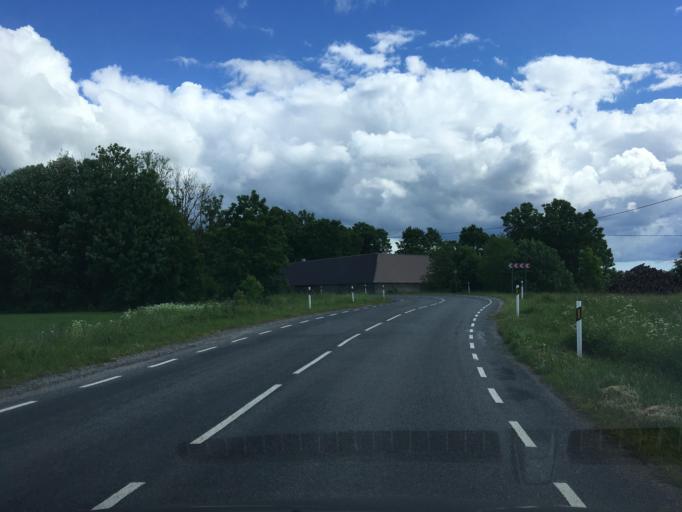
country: EE
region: Paernumaa
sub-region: Halinga vald
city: Parnu-Jaagupi
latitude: 58.6153
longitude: 24.4555
